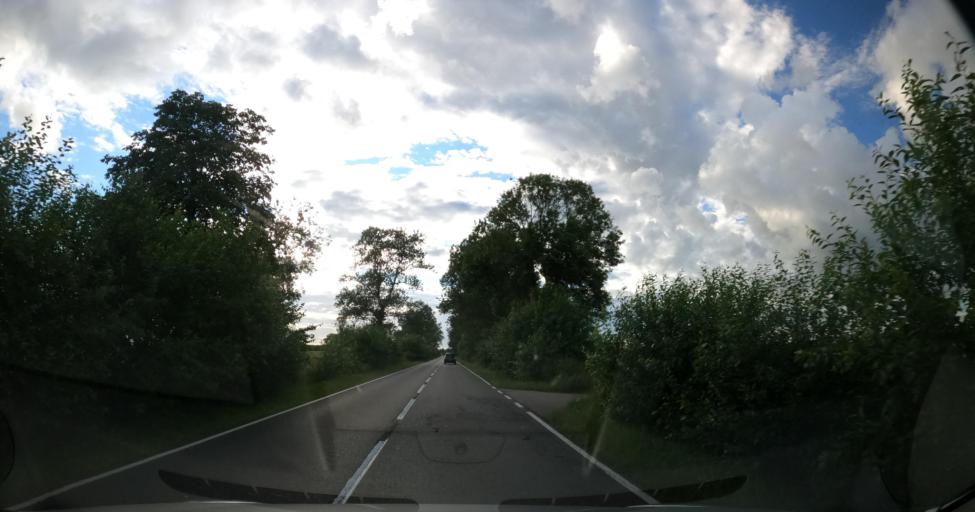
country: PL
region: Pomeranian Voivodeship
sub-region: Powiat slupski
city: Damnica
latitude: 54.4265
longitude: 17.3697
